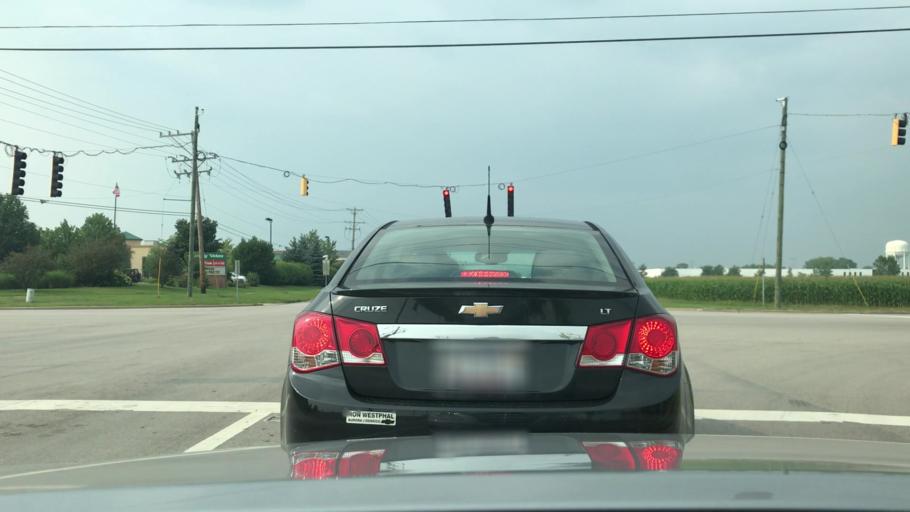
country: US
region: Illinois
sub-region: Will County
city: Plainfield
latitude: 41.6219
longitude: -88.2218
